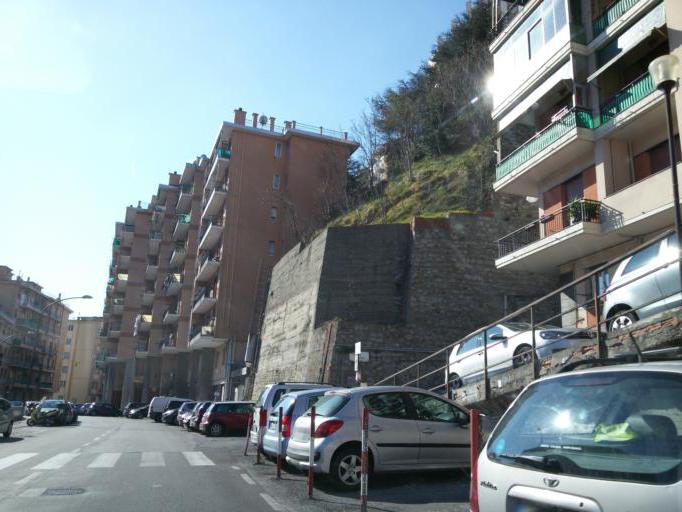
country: IT
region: Liguria
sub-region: Provincia di Genova
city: Genoa
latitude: 44.4248
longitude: 8.9153
